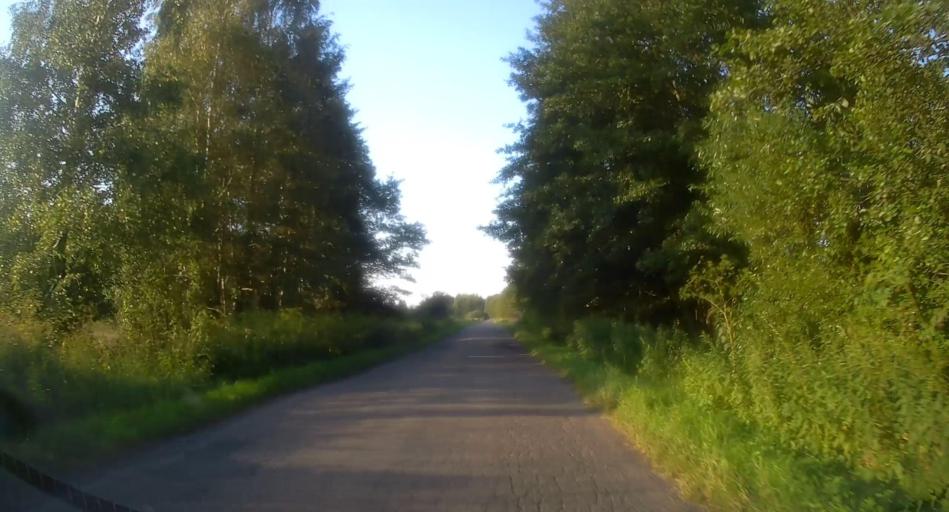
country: PL
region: Lodz Voivodeship
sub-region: Powiat skierniewicki
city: Kaweczyn Nowy
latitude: 51.8926
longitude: 20.2951
